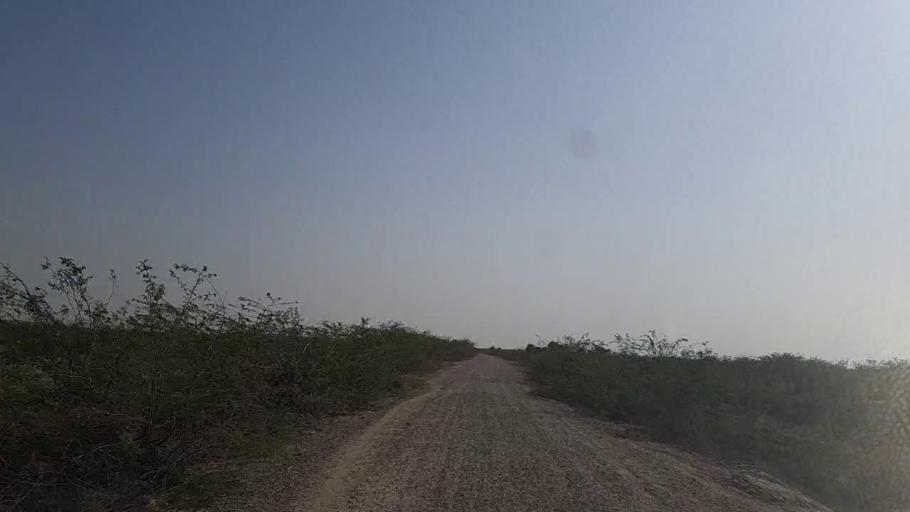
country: PK
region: Sindh
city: Naukot
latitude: 24.5948
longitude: 69.2631
